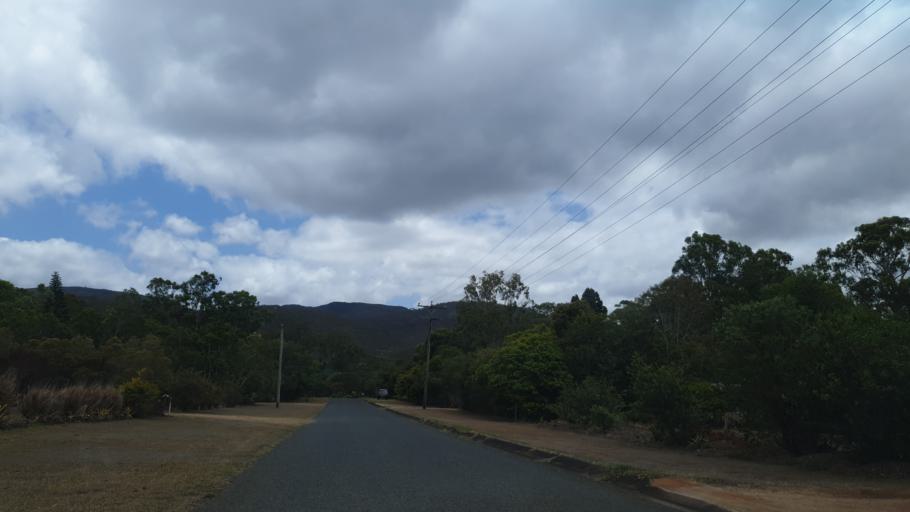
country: AU
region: Queensland
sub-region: Tablelands
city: Tolga
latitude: -17.2073
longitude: 145.4403
